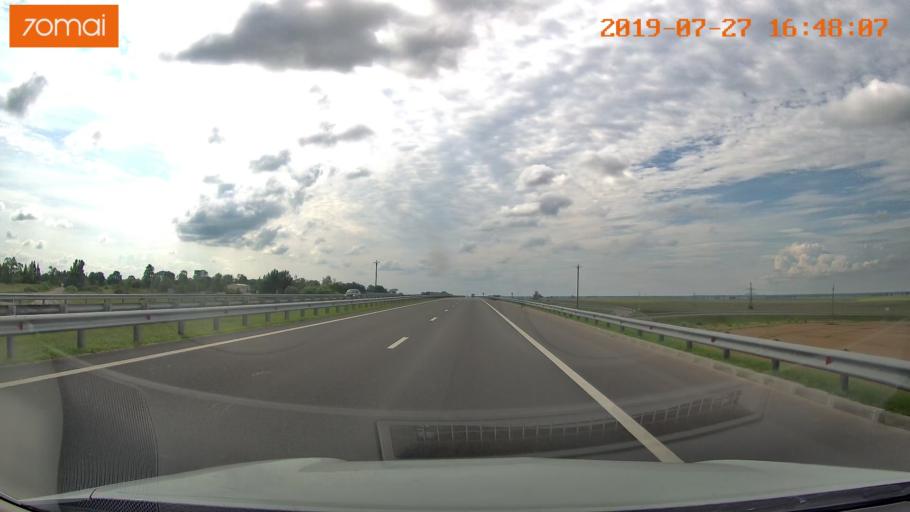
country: RU
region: Kaliningrad
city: Gvardeysk
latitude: 54.6696
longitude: 20.9762
